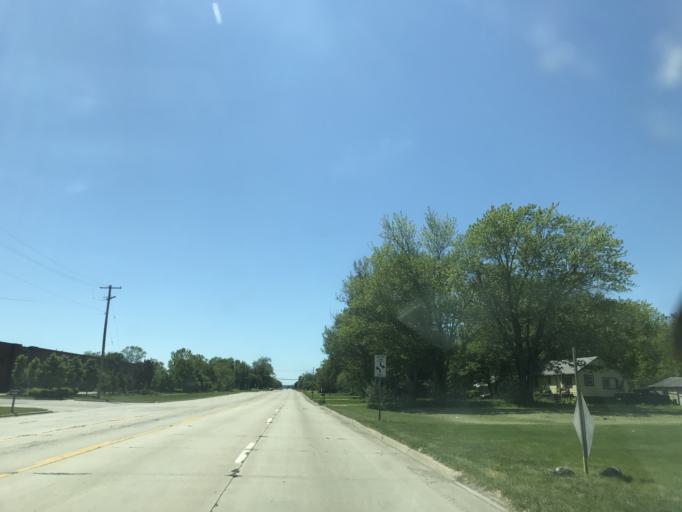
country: US
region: Michigan
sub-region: Wayne County
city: Taylor
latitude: 42.2102
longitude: -83.3128
